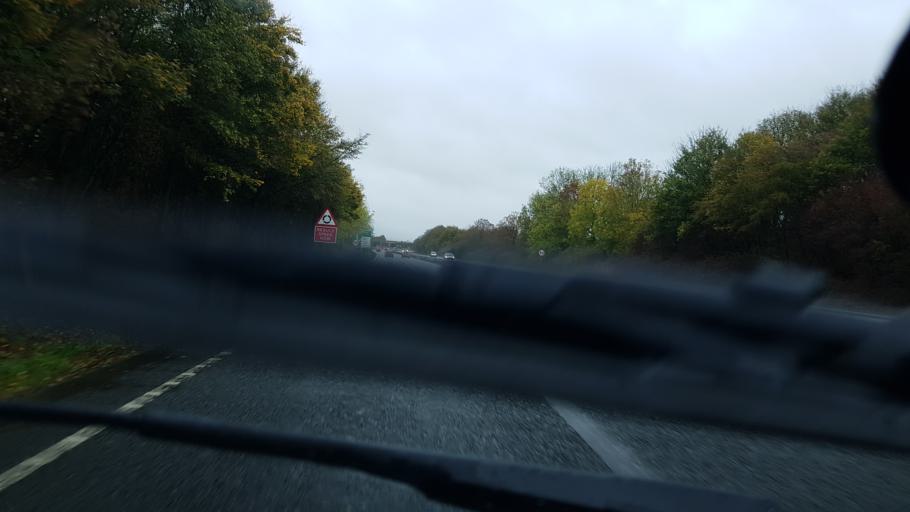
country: GB
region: England
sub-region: Oxfordshire
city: Witney
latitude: 51.7782
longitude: -1.5170
